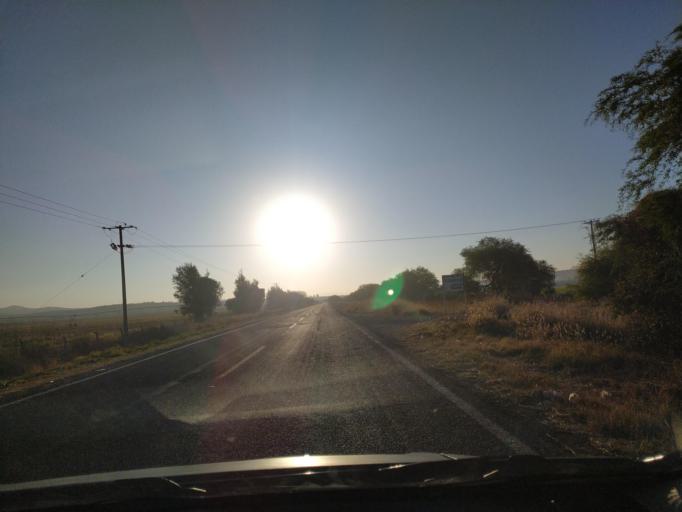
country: MX
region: Guanajuato
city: Ciudad Manuel Doblado
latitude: 20.7362
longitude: -101.8497
